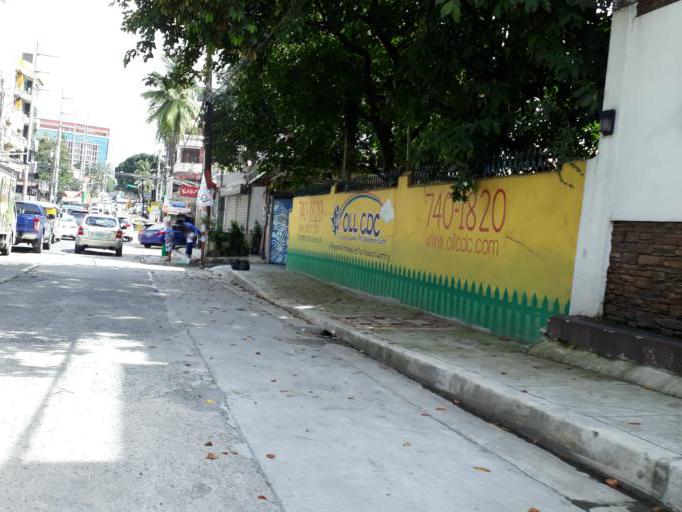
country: PH
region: Calabarzon
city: Del Monte
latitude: 14.6268
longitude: 121.0011
